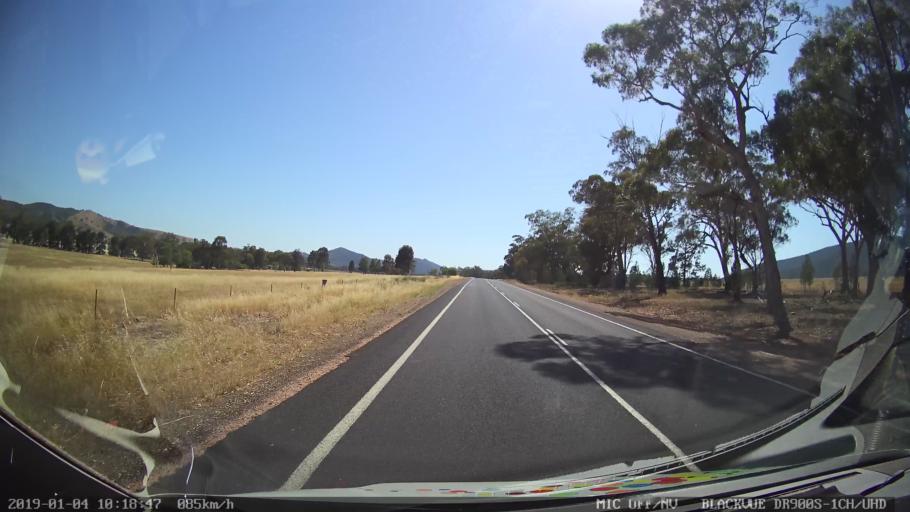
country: AU
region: New South Wales
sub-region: Cabonne
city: Canowindra
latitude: -33.3803
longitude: 148.4713
